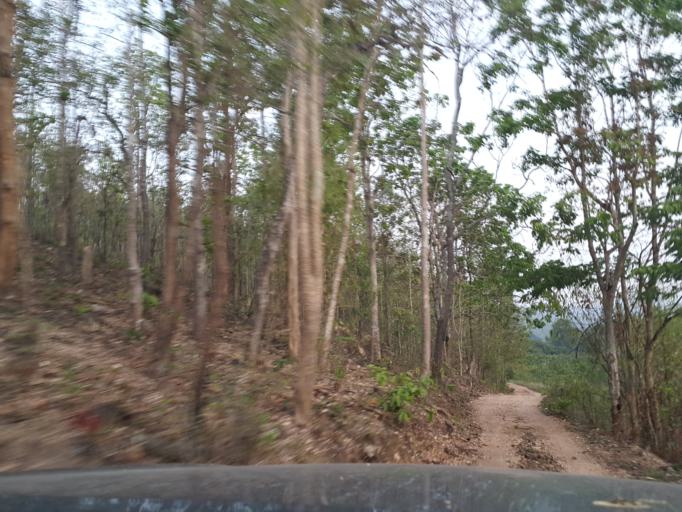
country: TH
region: Lamphun
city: Thung Hua Chang
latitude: 17.9002
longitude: 99.0820
